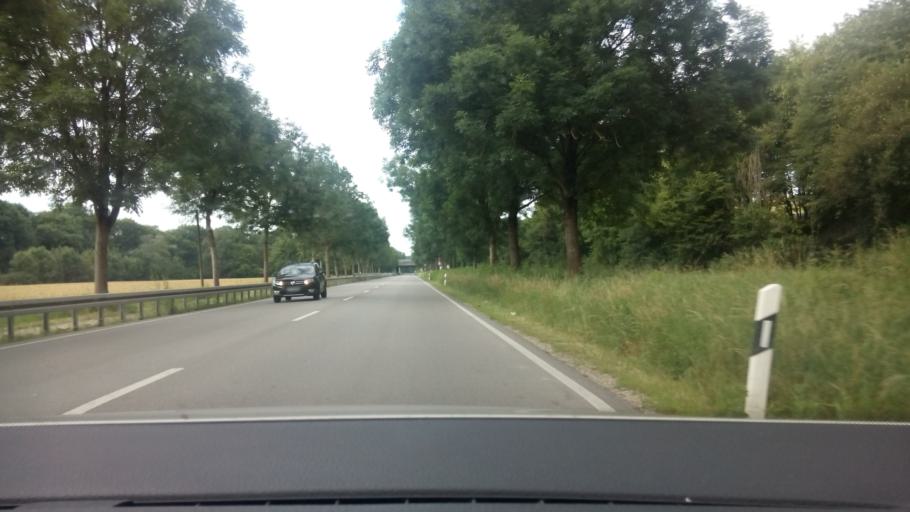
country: DE
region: Bavaria
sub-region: Upper Bavaria
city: Unterfoehring
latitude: 48.2217
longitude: 11.6381
